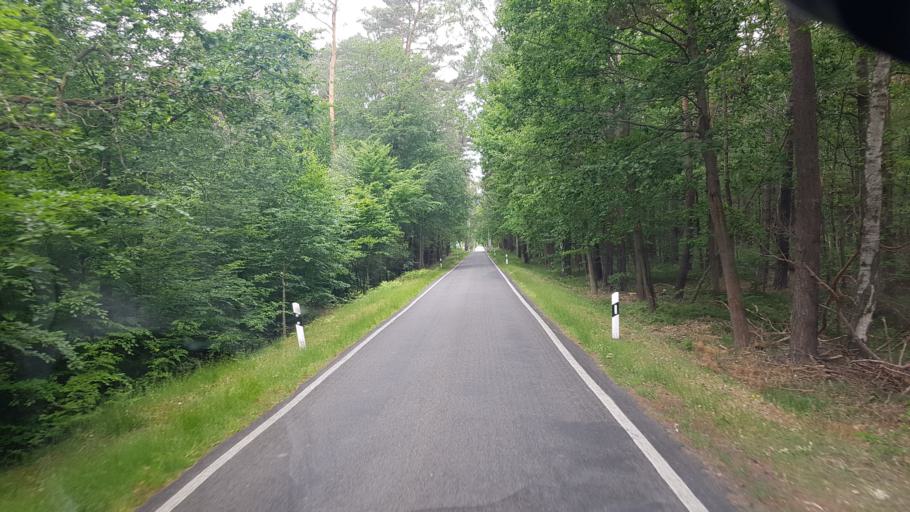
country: DE
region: Brandenburg
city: Lebusa
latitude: 51.7994
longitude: 13.4557
